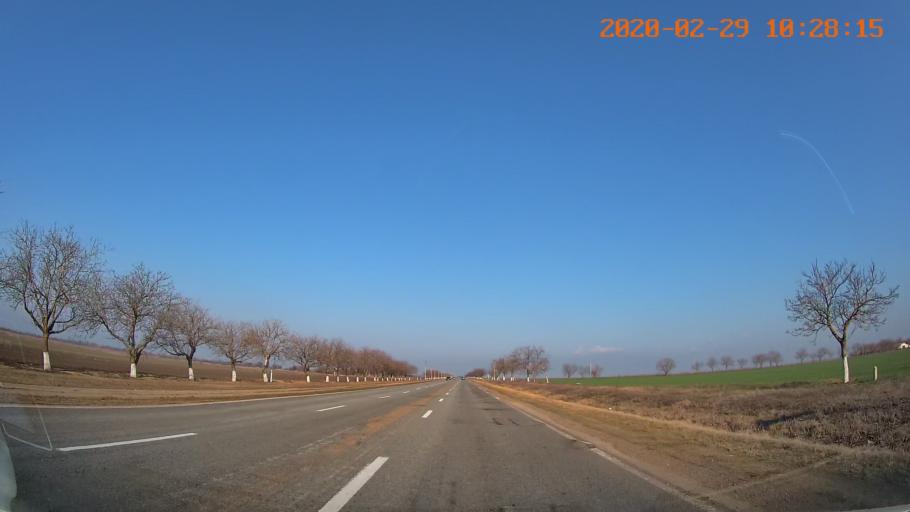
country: MD
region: Telenesti
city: Tiraspolul Nou
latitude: 46.9079
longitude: 29.5926
